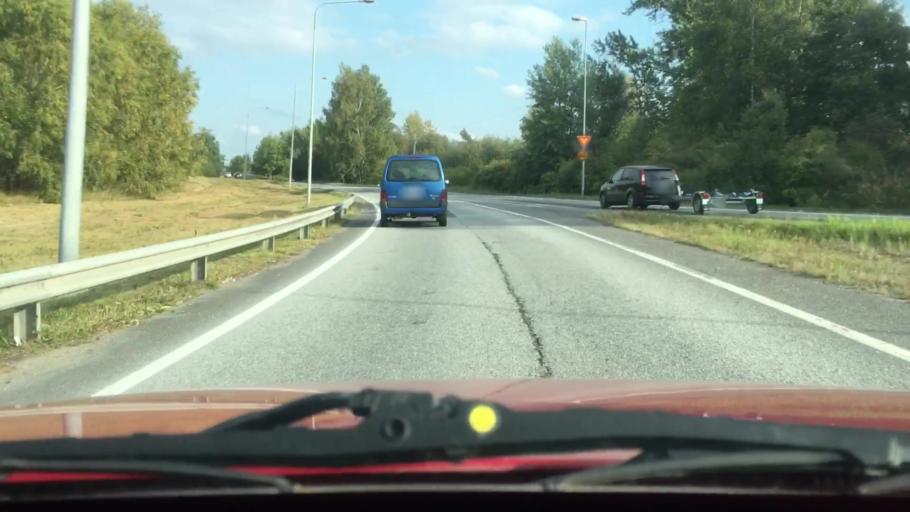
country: FI
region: Varsinais-Suomi
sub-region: Turku
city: Raisio
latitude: 60.4593
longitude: 22.2122
